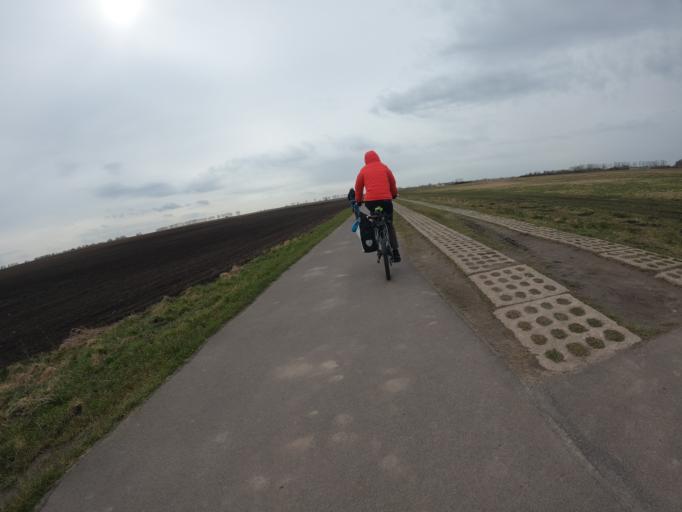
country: PL
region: West Pomeranian Voivodeship
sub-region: Powiat gryficki
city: Mrzezyno
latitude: 54.1070
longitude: 15.2917
